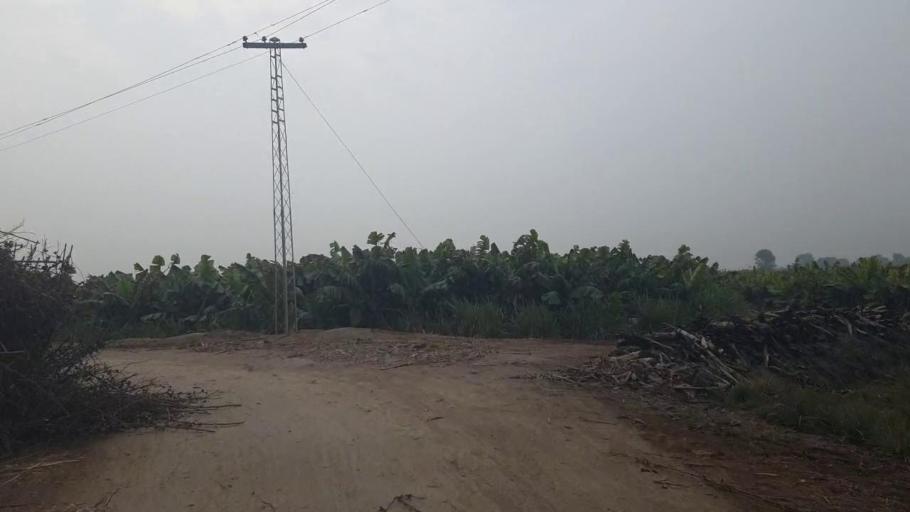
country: PK
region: Sindh
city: Tando Adam
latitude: 25.7028
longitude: 68.6432
